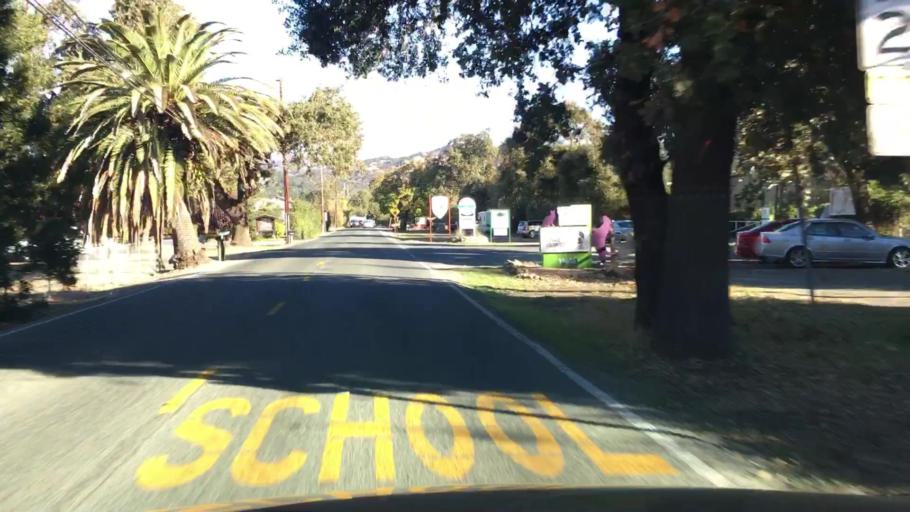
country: US
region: California
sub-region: Sonoma County
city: Sonoma
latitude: 38.2861
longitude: -122.4364
